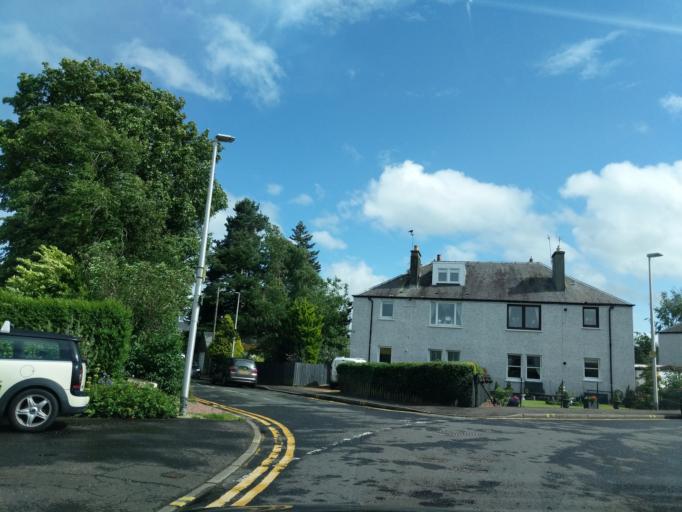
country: GB
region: Scotland
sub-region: Midlothian
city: Loanhead
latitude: 55.8587
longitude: -3.1635
